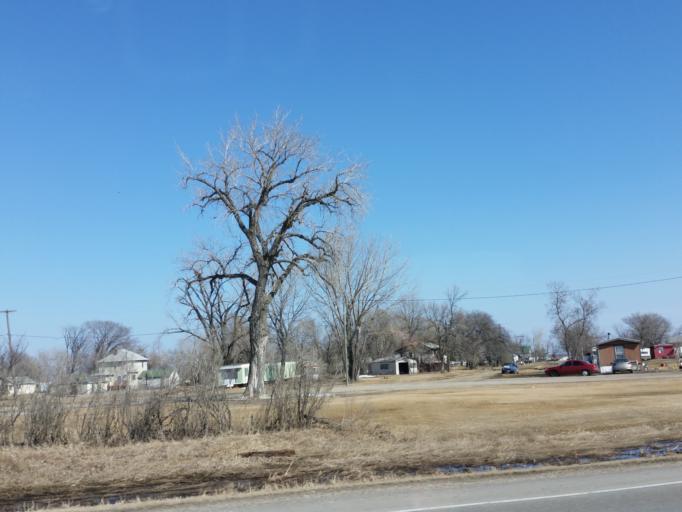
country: US
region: North Dakota
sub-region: Walsh County
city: Grafton
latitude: 48.2047
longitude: -97.3416
